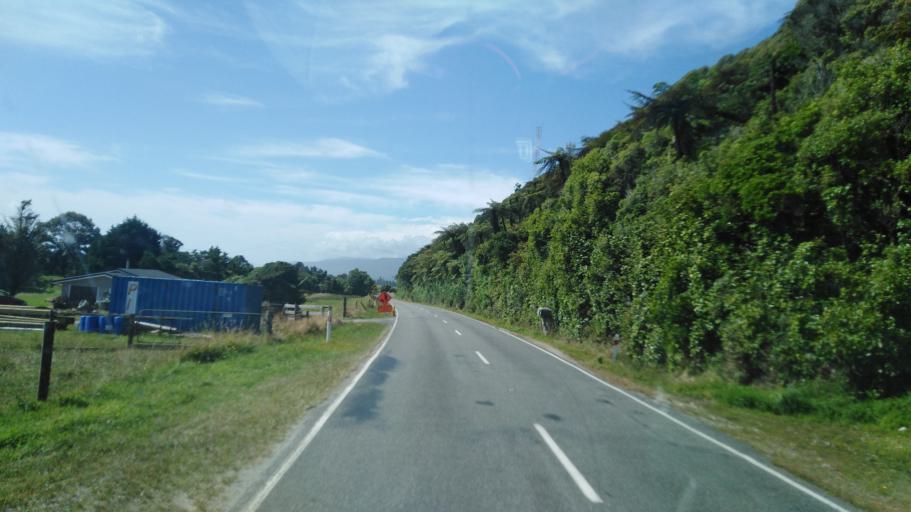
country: NZ
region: West Coast
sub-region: Buller District
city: Westport
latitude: -41.2596
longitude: 172.1127
